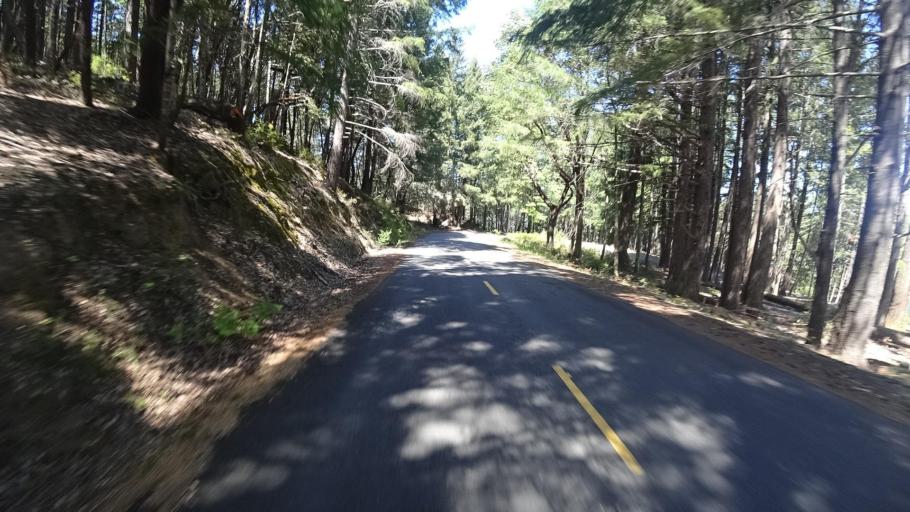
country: US
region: California
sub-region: Humboldt County
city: Rio Dell
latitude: 40.3244
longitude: -124.0517
